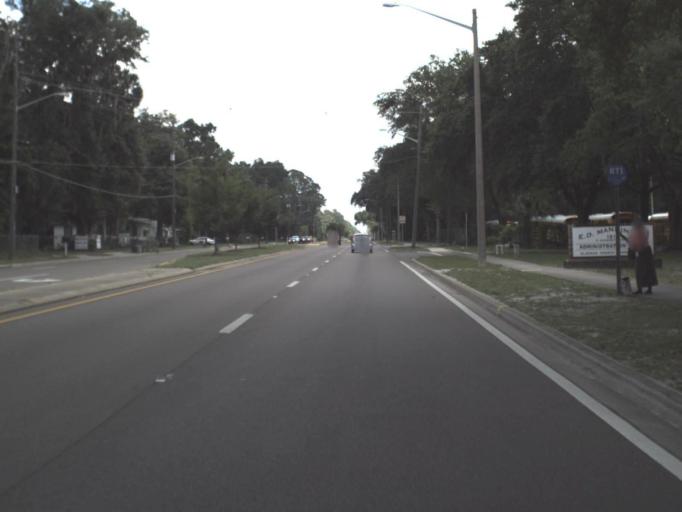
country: US
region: Florida
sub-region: Alachua County
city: Gainesville
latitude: 29.6518
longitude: -82.3015
